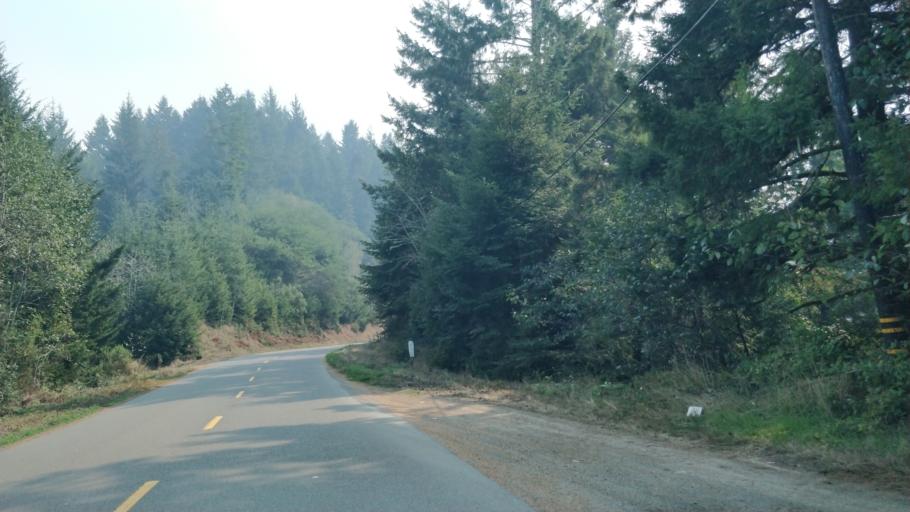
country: US
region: California
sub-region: Humboldt County
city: Ferndale
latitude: 40.5341
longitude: -124.2703
